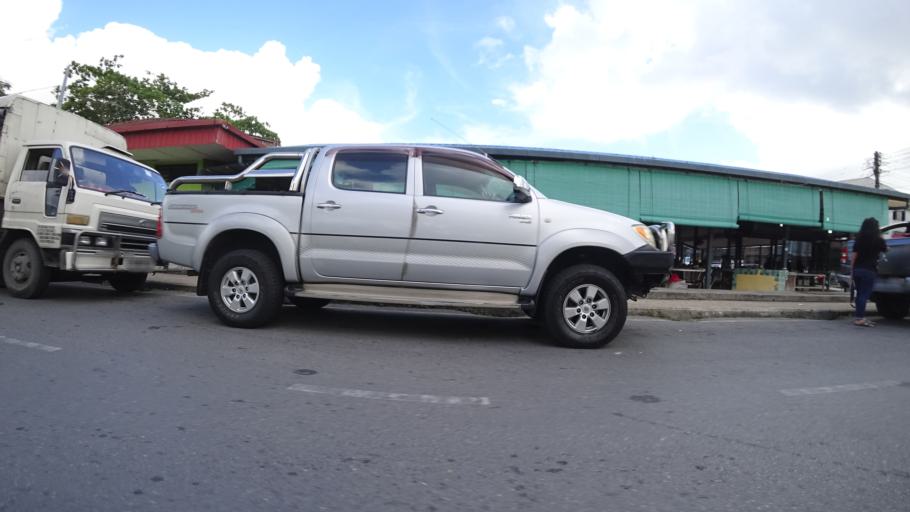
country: MY
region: Sarawak
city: Miri
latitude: 4.4673
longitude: 114.0078
